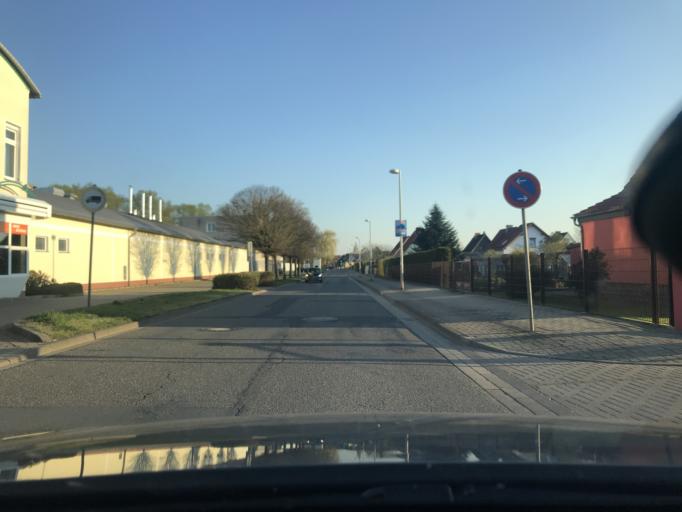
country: DE
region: Thuringia
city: Nordhausen
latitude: 51.5004
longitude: 10.7699
